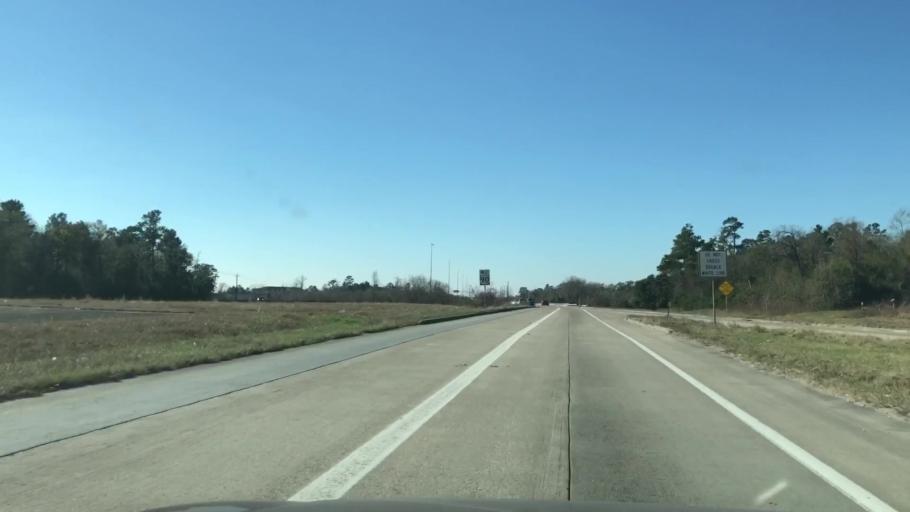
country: US
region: Texas
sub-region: Harris County
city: Jacinto City
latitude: 29.8125
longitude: -95.2110
